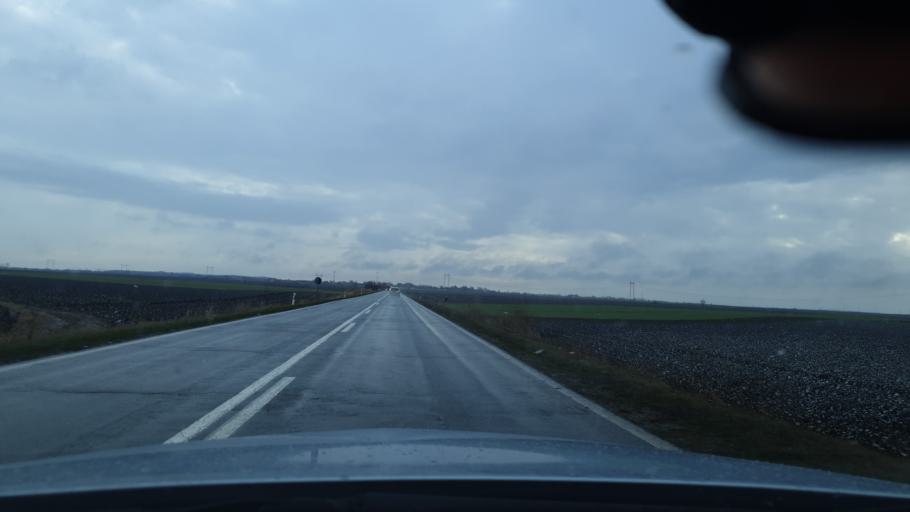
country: RS
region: Autonomna Pokrajina Vojvodina
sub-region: Juznobanatski Okrug
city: Kovin
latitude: 44.8298
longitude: 20.8351
